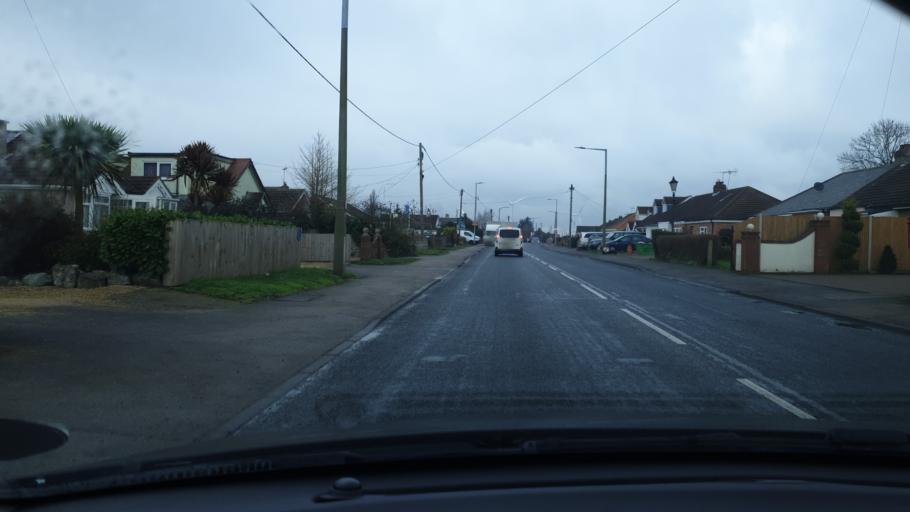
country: GB
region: England
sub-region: Essex
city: Saint Osyth
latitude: 51.7969
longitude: 1.1192
